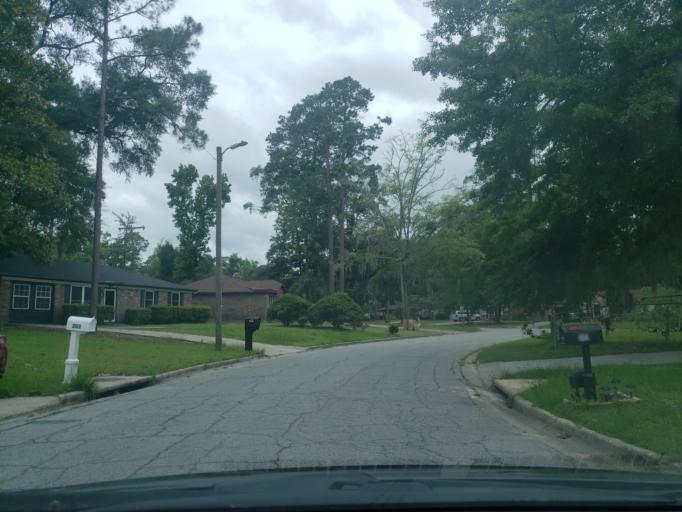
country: US
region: Georgia
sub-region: Chatham County
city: Montgomery
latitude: 31.9914
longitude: -81.1195
